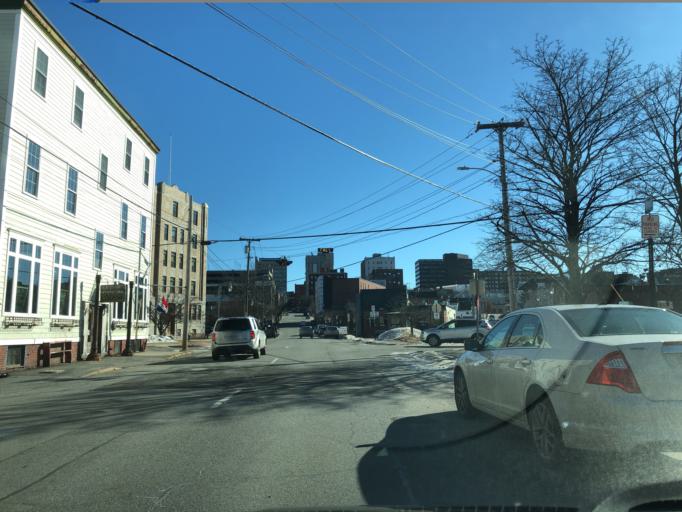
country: US
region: Maine
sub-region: Cumberland County
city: Portland
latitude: 43.6608
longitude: -70.2641
